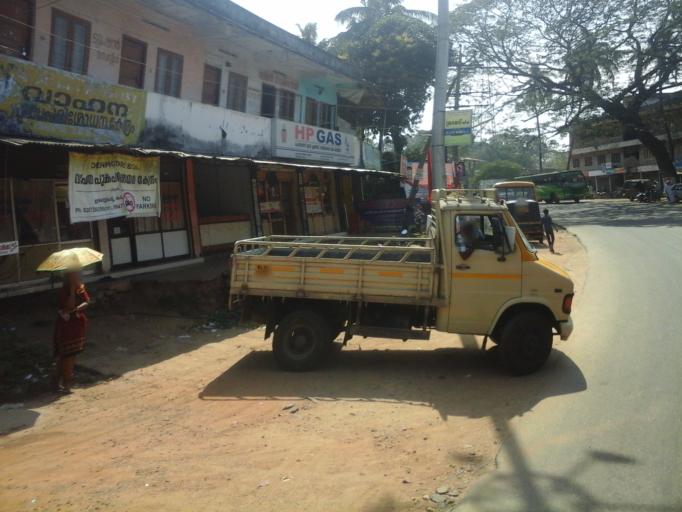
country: IN
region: Kerala
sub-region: Kottayam
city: Erattupetta
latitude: 9.6930
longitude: 76.7738
